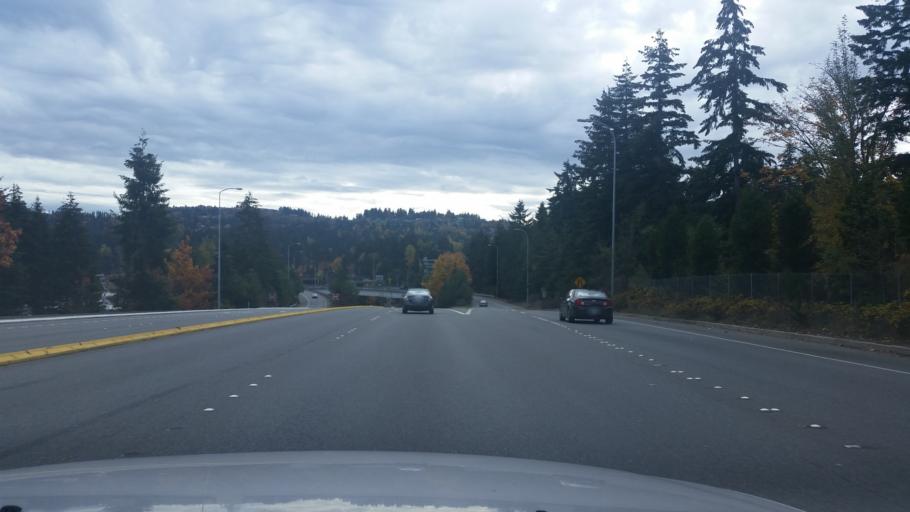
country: US
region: Washington
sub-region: King County
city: Eastgate
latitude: 47.5846
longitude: -122.1429
